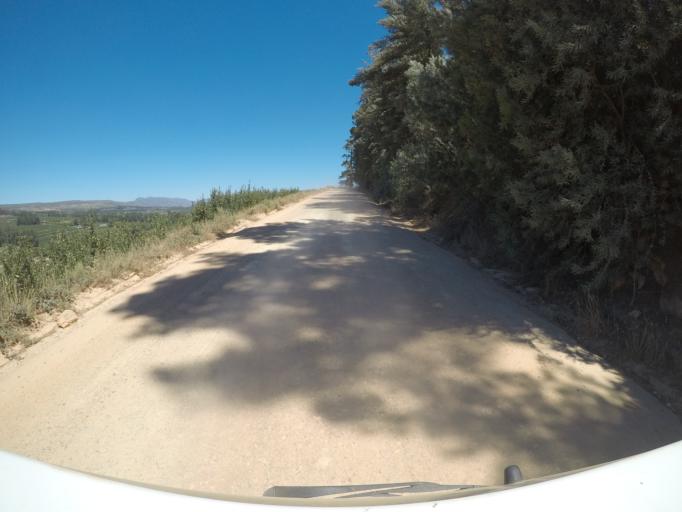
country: ZA
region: Western Cape
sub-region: Overberg District Municipality
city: Grabouw
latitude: -34.2426
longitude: 19.0888
